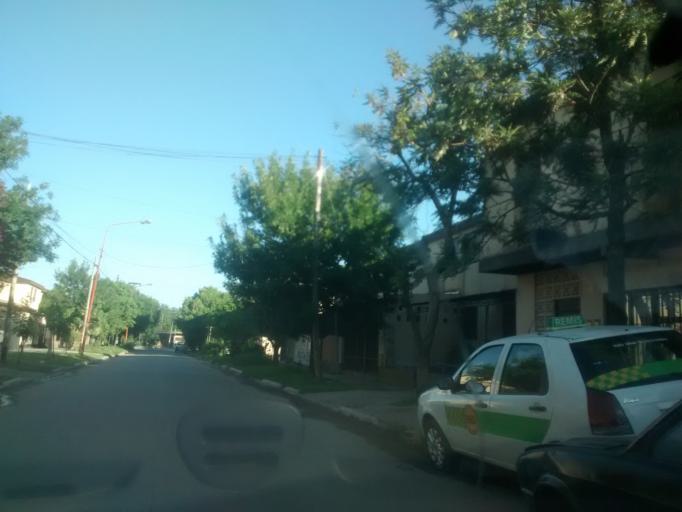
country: AR
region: Chaco
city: Resistencia
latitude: -27.4572
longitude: -59.0201
